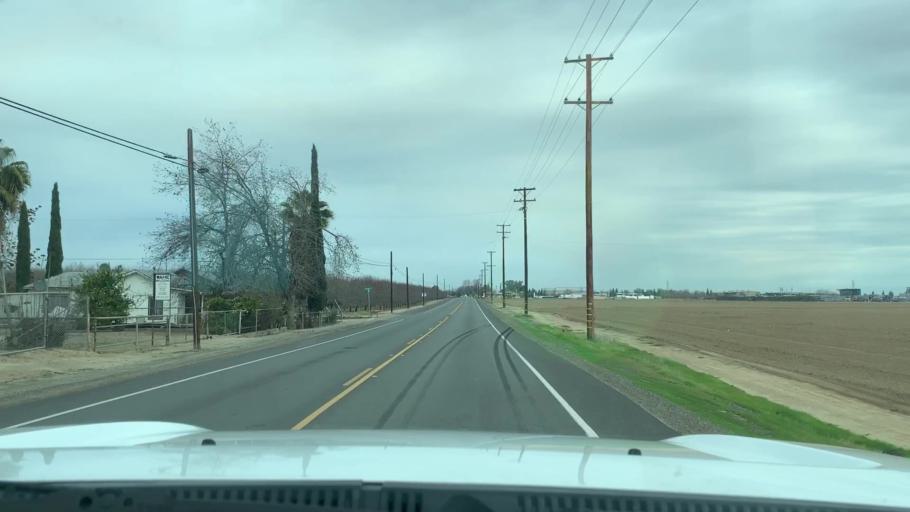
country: US
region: California
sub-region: Kern County
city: Shafter
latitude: 35.4339
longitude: -119.2518
